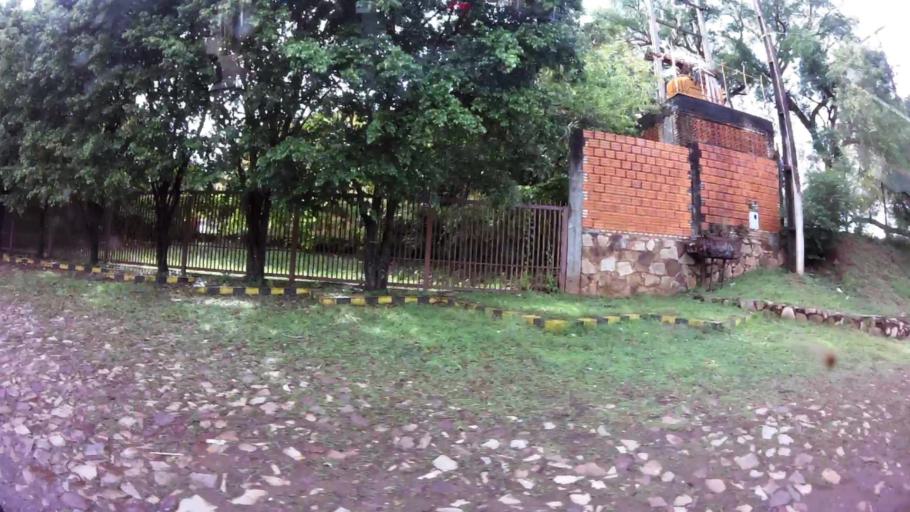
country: PY
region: Central
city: Limpio
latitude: -25.1595
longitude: -57.4651
